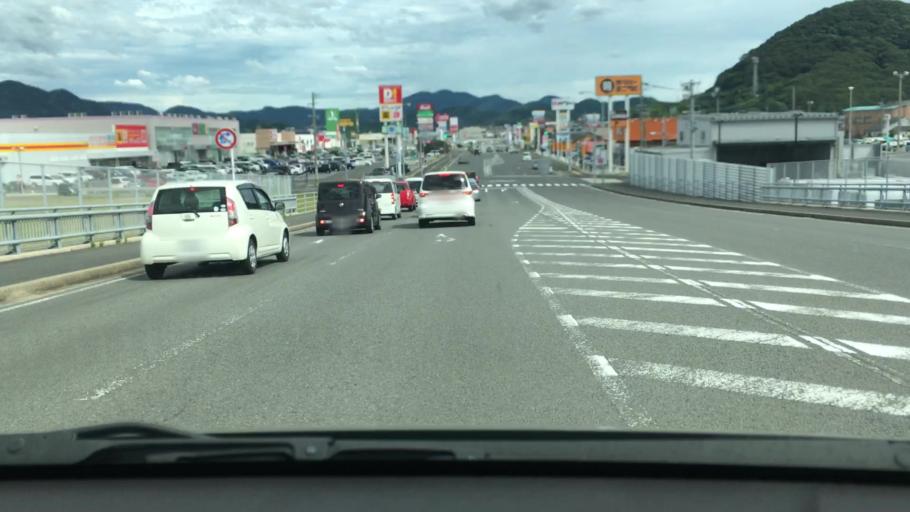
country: JP
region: Nagasaki
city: Togitsu
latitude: 32.8531
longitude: 129.8244
